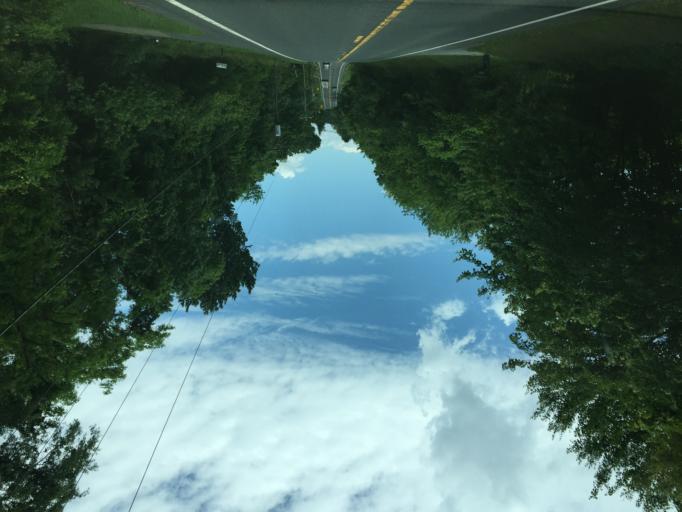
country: US
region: Pennsylvania
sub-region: York County
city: Susquehanna Trails
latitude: 39.6745
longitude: -76.3588
